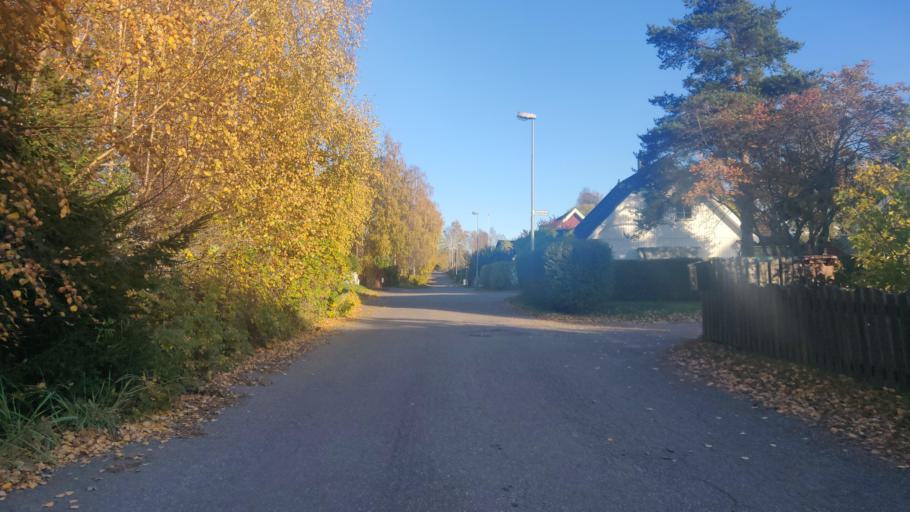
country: SE
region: Vaesternorrland
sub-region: Sundsvalls Kommun
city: Skottsund
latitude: 62.2883
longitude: 17.3846
